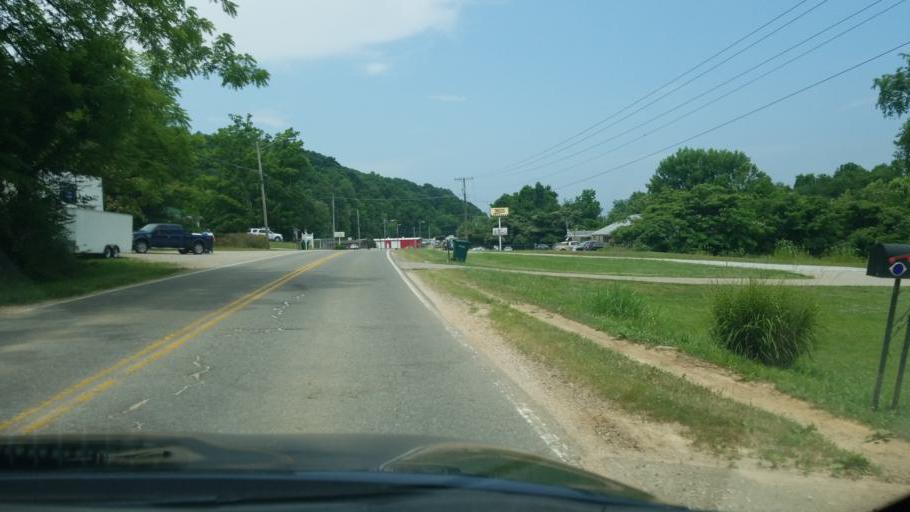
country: US
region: Tennessee
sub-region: Humphreys County
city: Waverly
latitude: 36.0790
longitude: -87.8320
